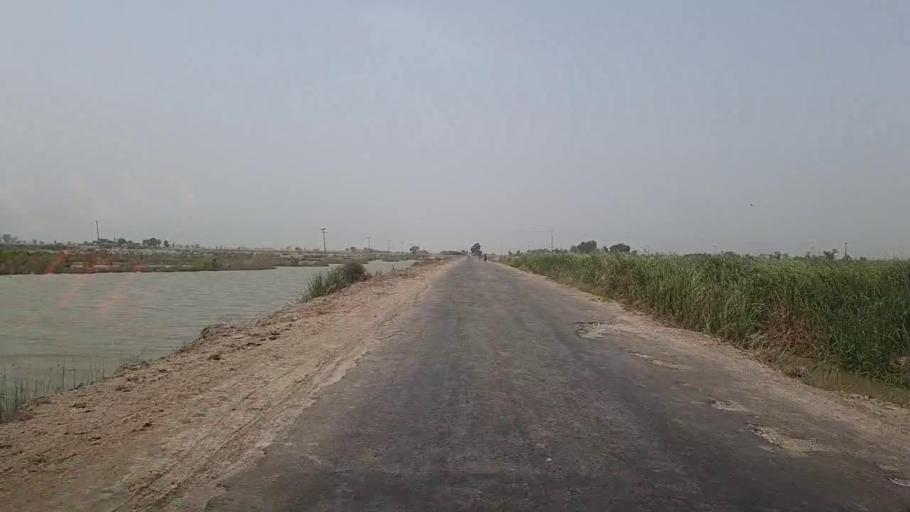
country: PK
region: Sindh
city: Radhan
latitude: 27.1495
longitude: 67.9380
